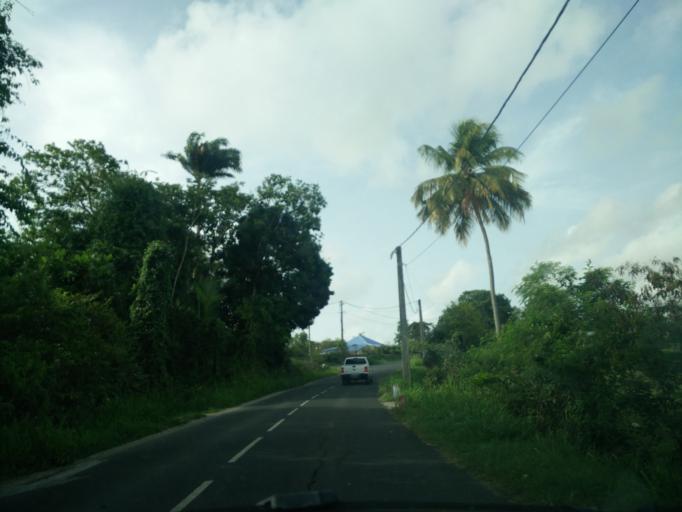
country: GP
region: Guadeloupe
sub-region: Guadeloupe
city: Le Moule
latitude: 16.2984
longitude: -61.3669
